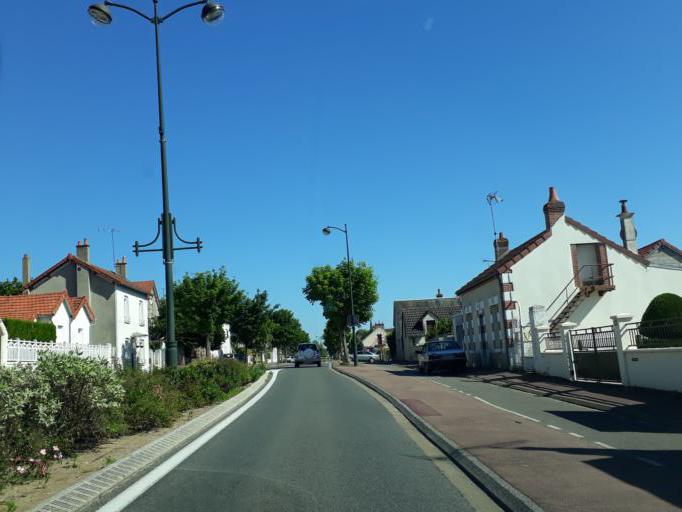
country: FR
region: Centre
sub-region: Departement du Loiret
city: Briare
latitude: 47.6513
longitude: 2.7253
